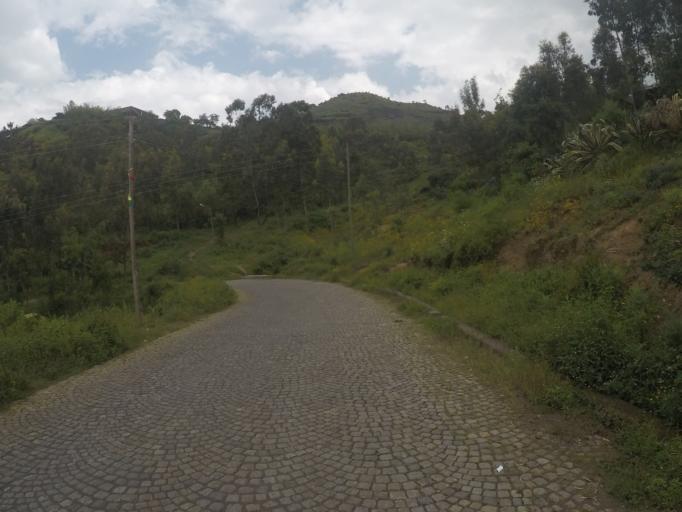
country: ET
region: Amhara
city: Lalibela
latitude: 12.0301
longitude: 39.0476
